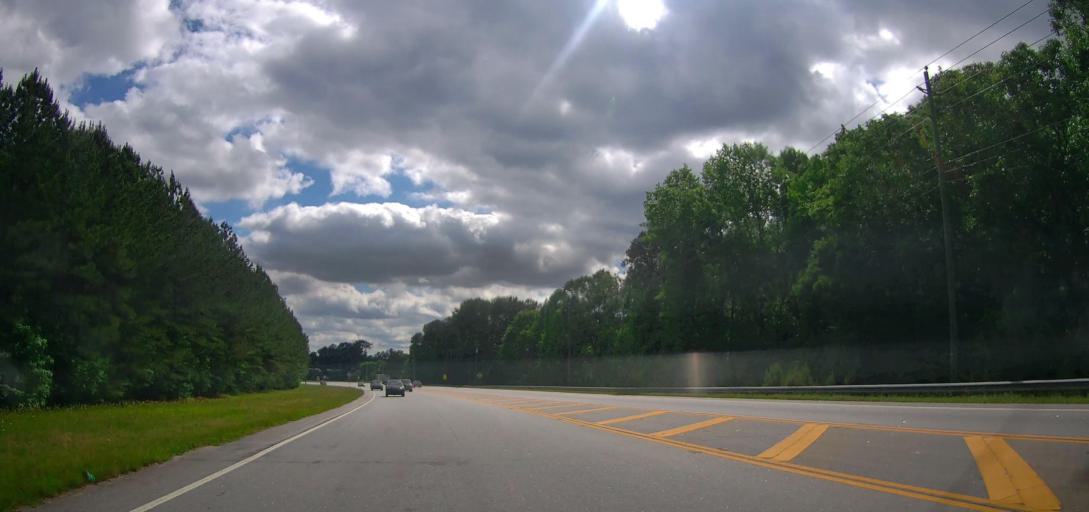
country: US
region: Georgia
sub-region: Rockdale County
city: Conyers
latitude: 33.6963
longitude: -83.9577
